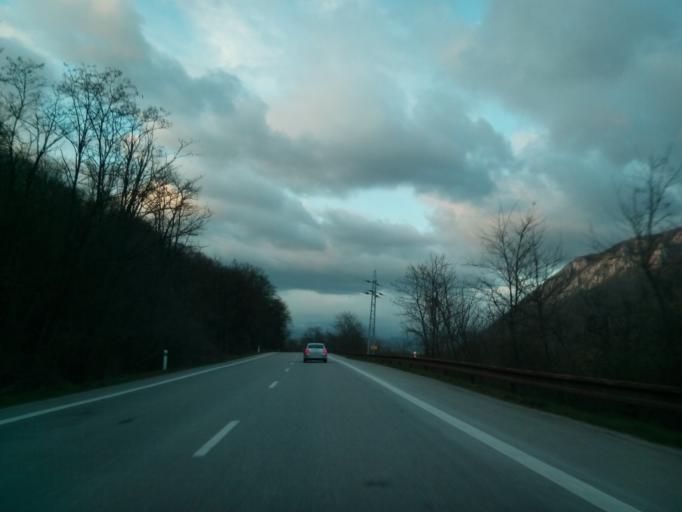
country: SK
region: Kosicky
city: Roznava
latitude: 48.5933
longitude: 20.4711
